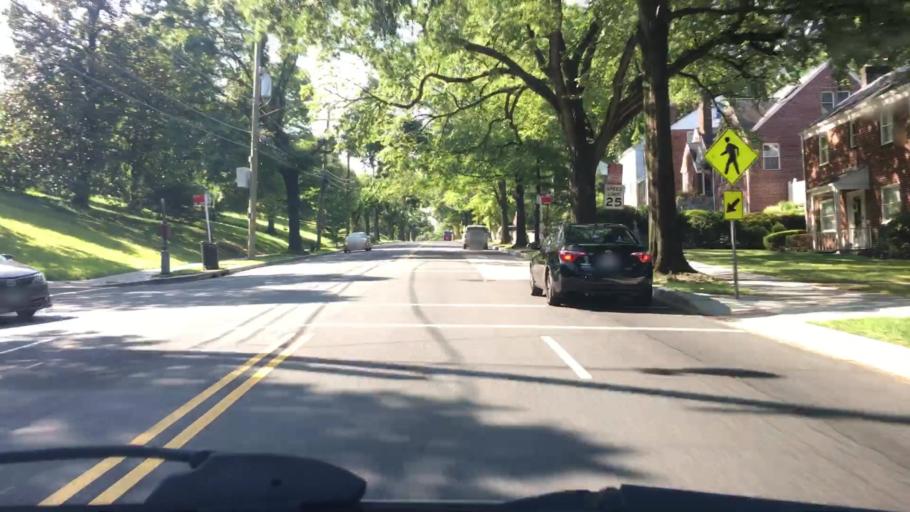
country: US
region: Maryland
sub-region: Prince George's County
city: Silver Hill
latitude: 38.8655
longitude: -76.9598
